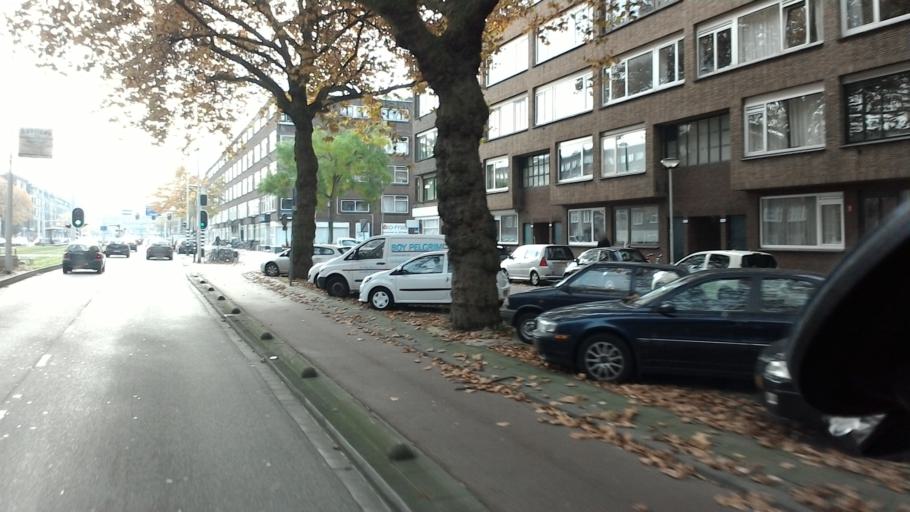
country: NL
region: South Holland
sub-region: Gemeente Rotterdam
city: Rotterdam
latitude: 51.9354
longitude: 4.4638
